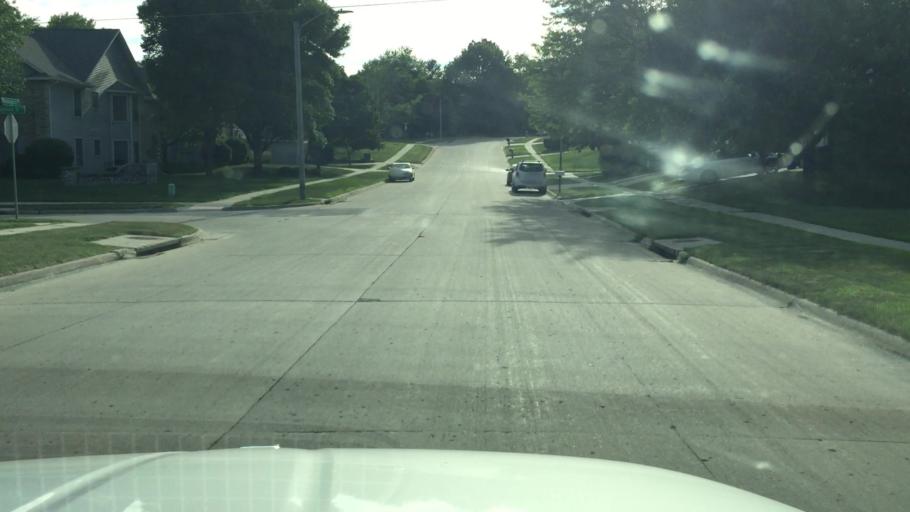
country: US
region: Iowa
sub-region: Johnson County
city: Iowa City
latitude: 41.6601
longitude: -91.4828
